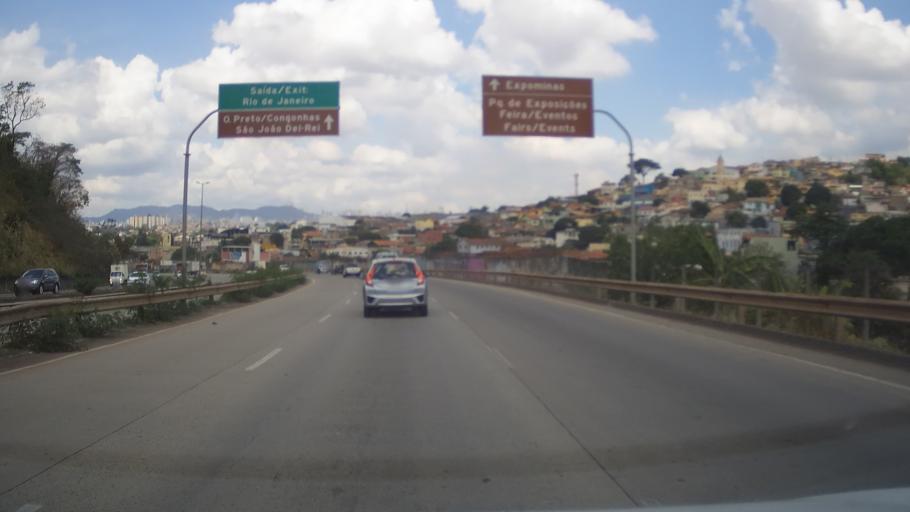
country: BR
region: Minas Gerais
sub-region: Contagem
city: Contagem
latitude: -19.9324
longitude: -44.0135
